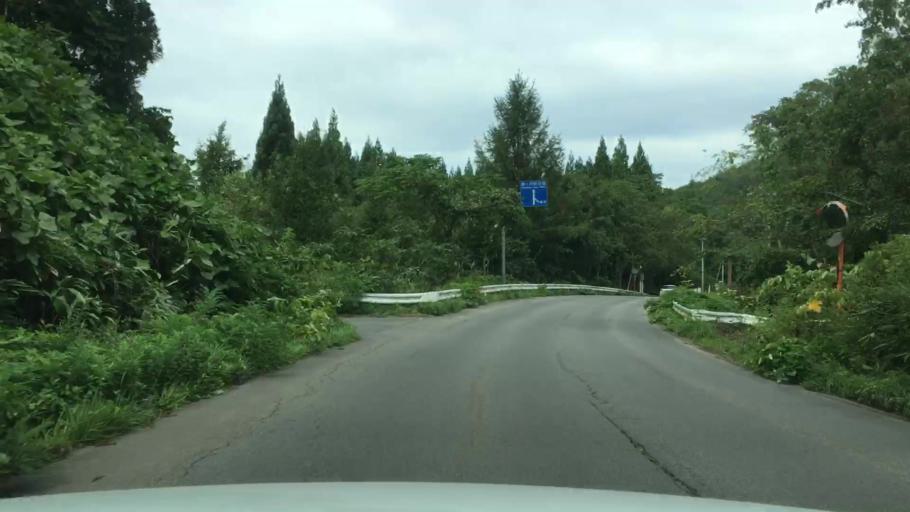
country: JP
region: Aomori
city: Shimokizukuri
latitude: 40.7201
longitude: 140.2585
